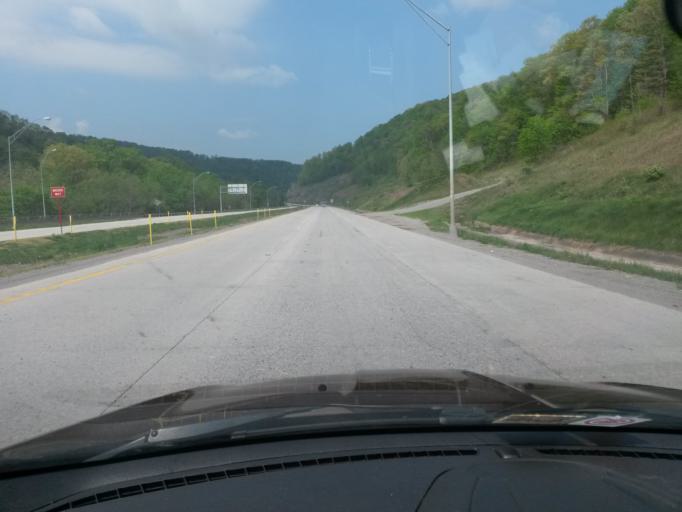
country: US
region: West Virginia
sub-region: Randolph County
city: Elkins
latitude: 38.9369
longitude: -79.9149
